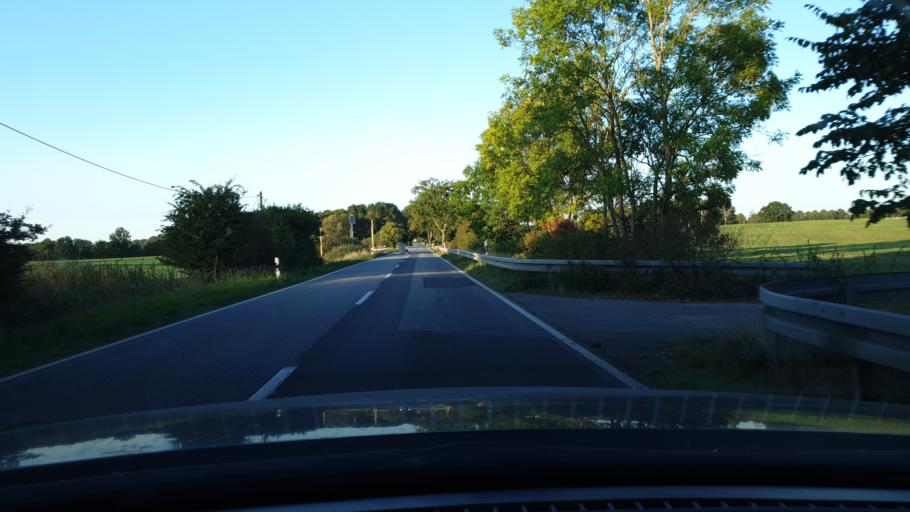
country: DE
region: Mecklenburg-Vorpommern
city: Lutzow
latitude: 53.6107
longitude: 11.1423
